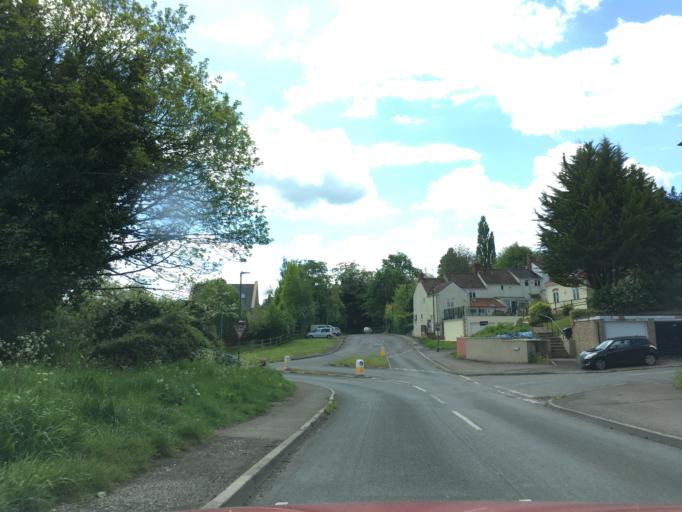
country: GB
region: England
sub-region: Gloucestershire
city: Dursley
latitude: 51.6916
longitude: -2.3558
